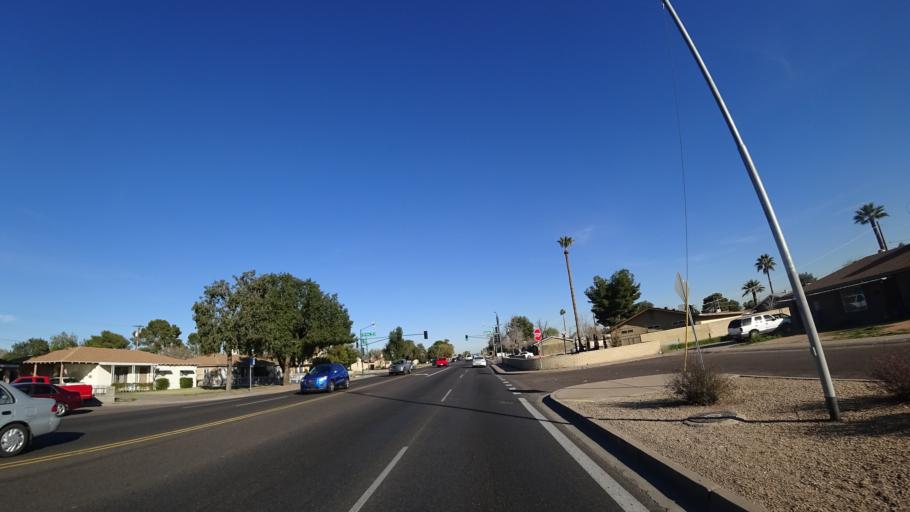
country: US
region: Arizona
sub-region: Maricopa County
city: Glendale
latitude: 33.5239
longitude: -112.1266
